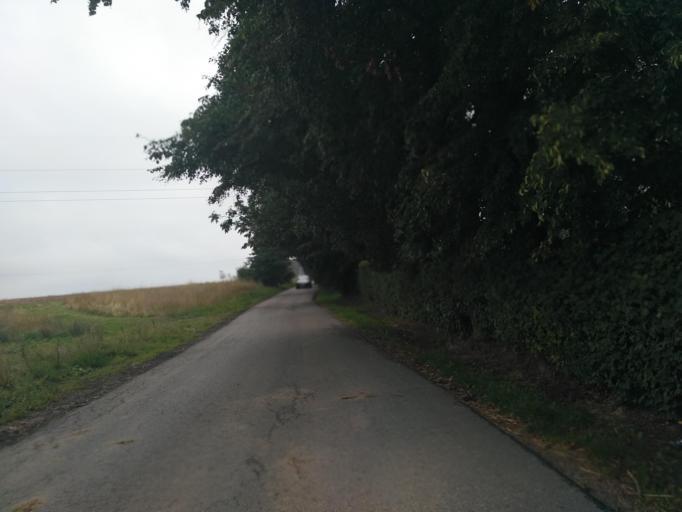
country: PL
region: Subcarpathian Voivodeship
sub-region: Powiat rzeszowski
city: Tyczyn
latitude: 49.9630
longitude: 22.0000
